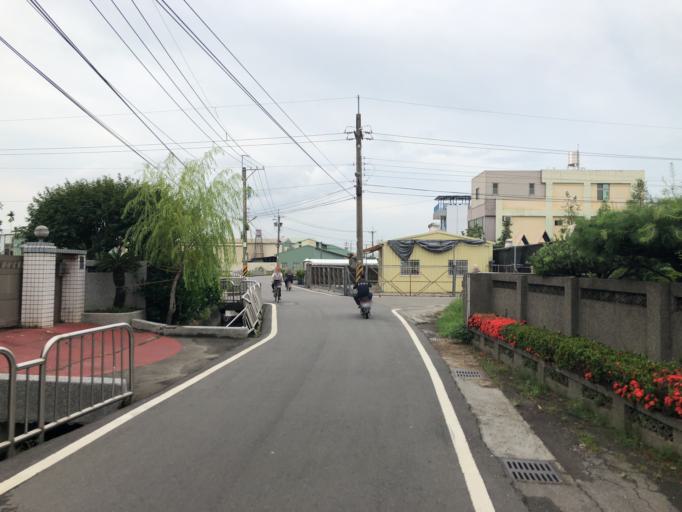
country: TW
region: Taiwan
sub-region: Taichung City
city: Taichung
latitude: 24.0633
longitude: 120.6818
